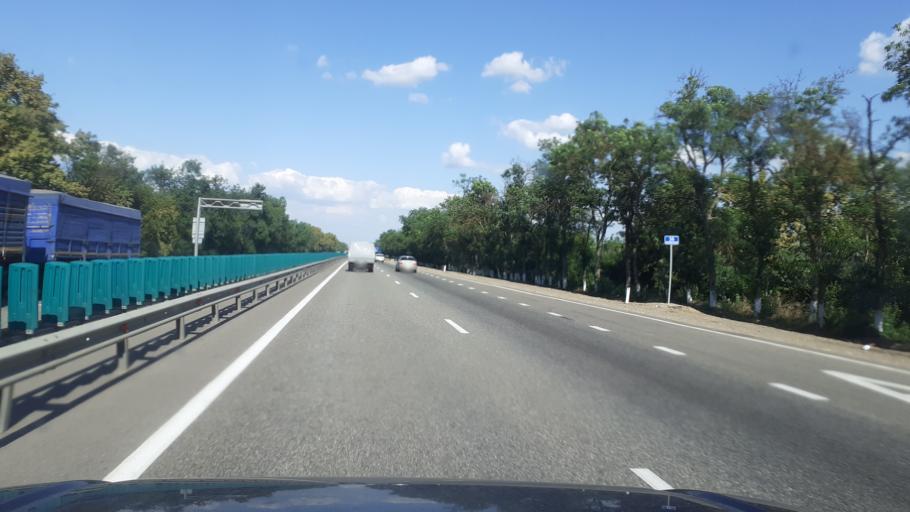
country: RU
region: Krasnodarskiy
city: Afipskiy
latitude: 44.8806
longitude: 38.7740
